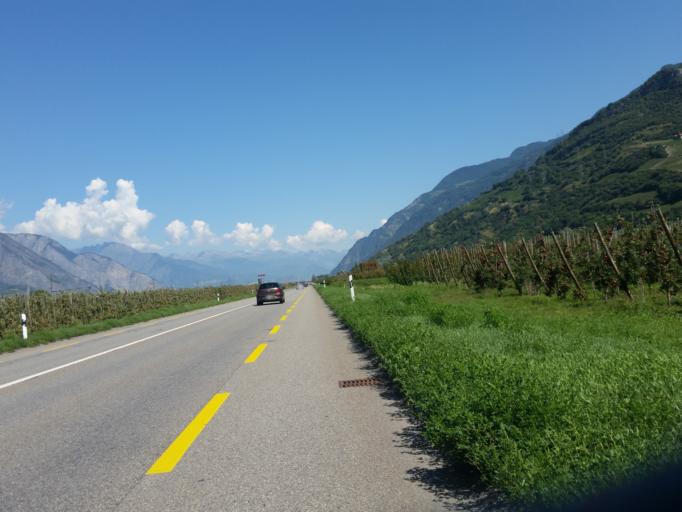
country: CH
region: Valais
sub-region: Martigny District
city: Charrat-les-Chenes
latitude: 46.1325
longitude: 7.1398
